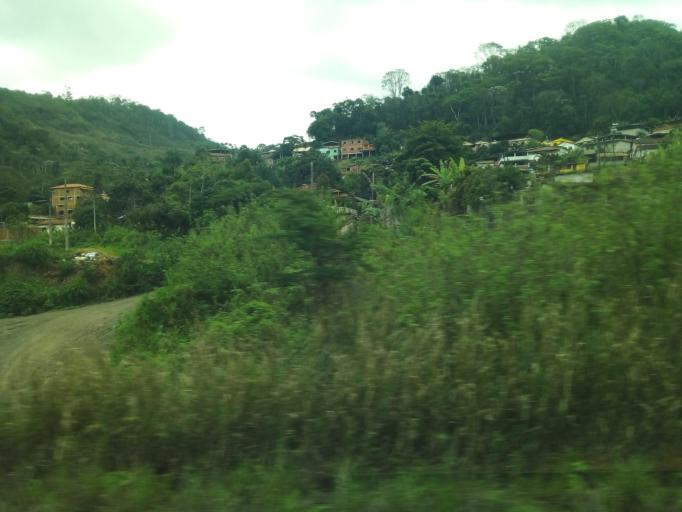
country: BR
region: Minas Gerais
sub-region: Joao Monlevade
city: Joao Monlevade
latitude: -19.8535
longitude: -43.1208
